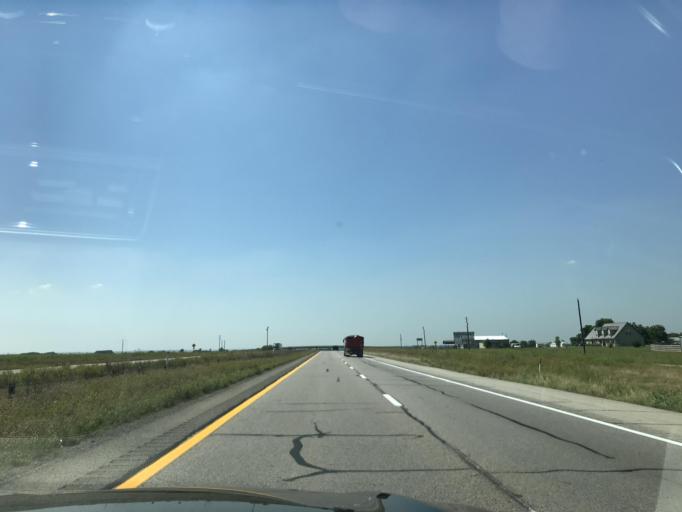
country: US
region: Texas
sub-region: Johnson County
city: Grandview
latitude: 32.3295
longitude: -97.1887
